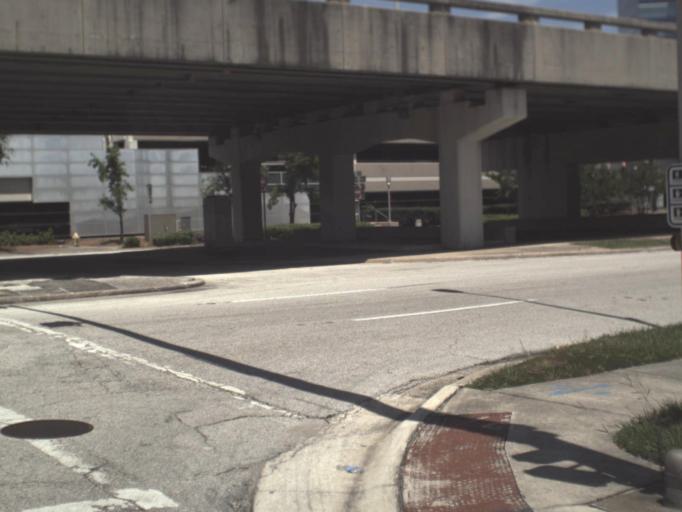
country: US
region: Florida
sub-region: Duval County
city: Jacksonville
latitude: 30.3163
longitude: -81.6588
